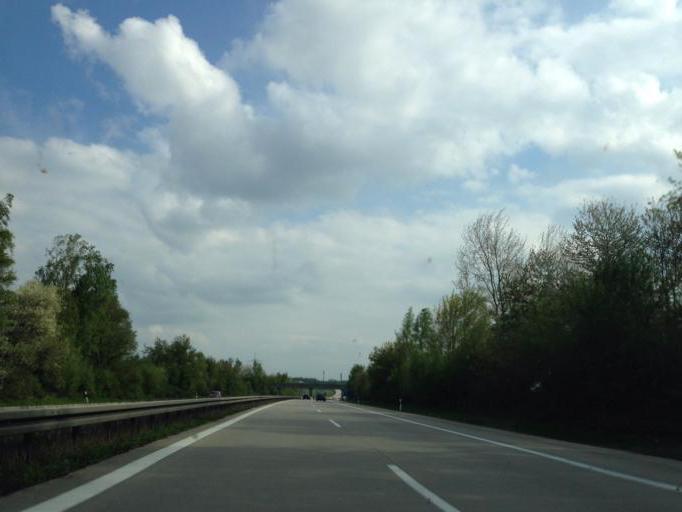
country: DE
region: Saxony
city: Mochau
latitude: 51.1269
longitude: 13.1680
